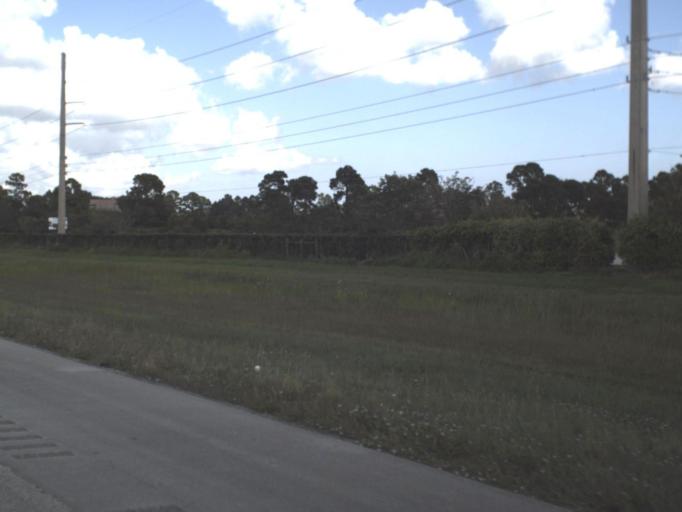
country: US
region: Florida
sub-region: Martin County
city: North River Shores
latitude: 27.1904
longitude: -80.3241
